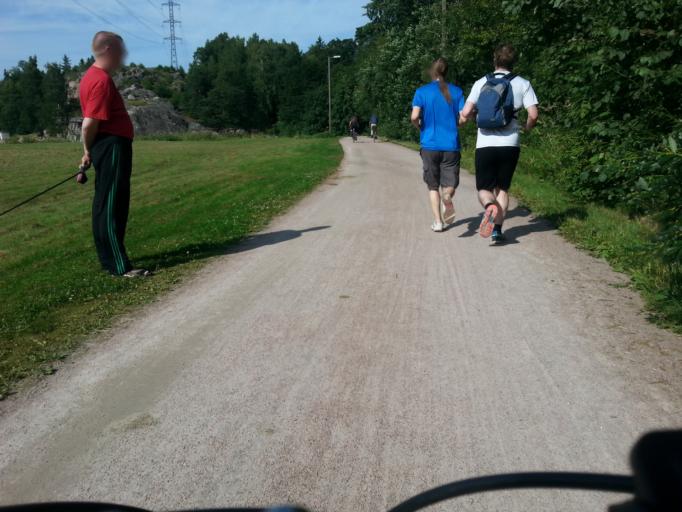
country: FI
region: Uusimaa
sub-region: Helsinki
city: Helsinki
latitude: 60.2263
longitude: 24.9850
